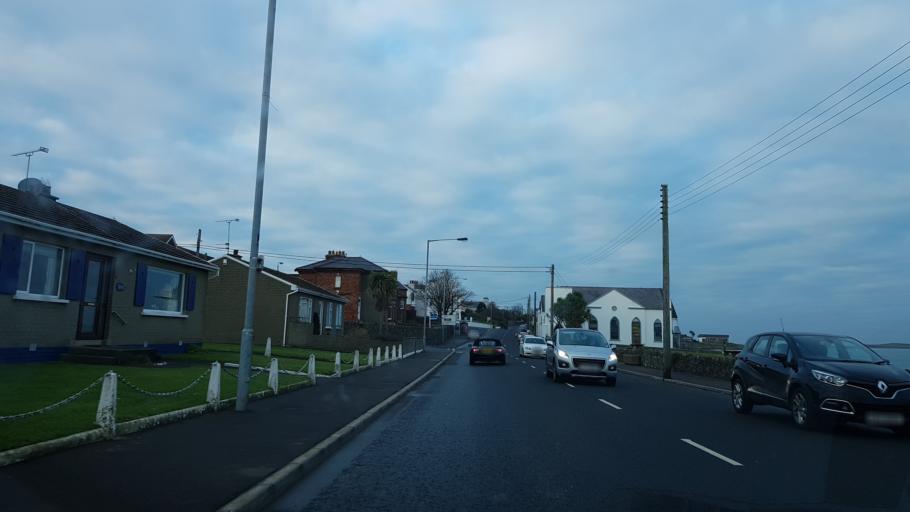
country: GB
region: Northern Ireland
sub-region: Down District
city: Donaghadee
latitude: 54.6451
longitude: -5.5397
